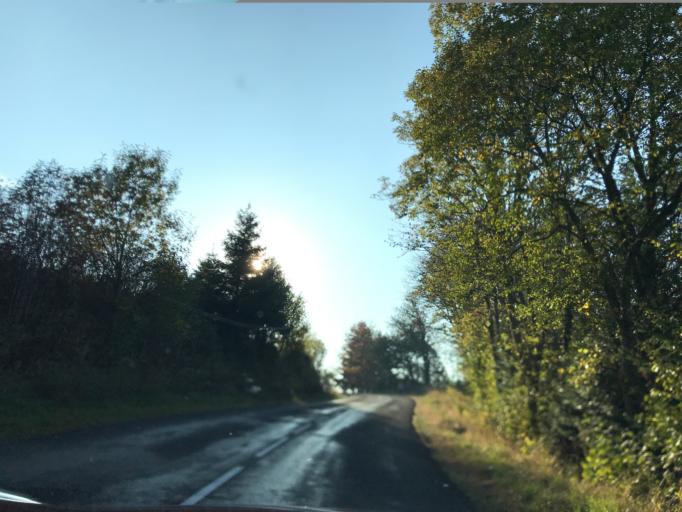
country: FR
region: Rhone-Alpes
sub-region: Departement de la Loire
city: Noiretable
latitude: 45.7893
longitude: 3.6891
